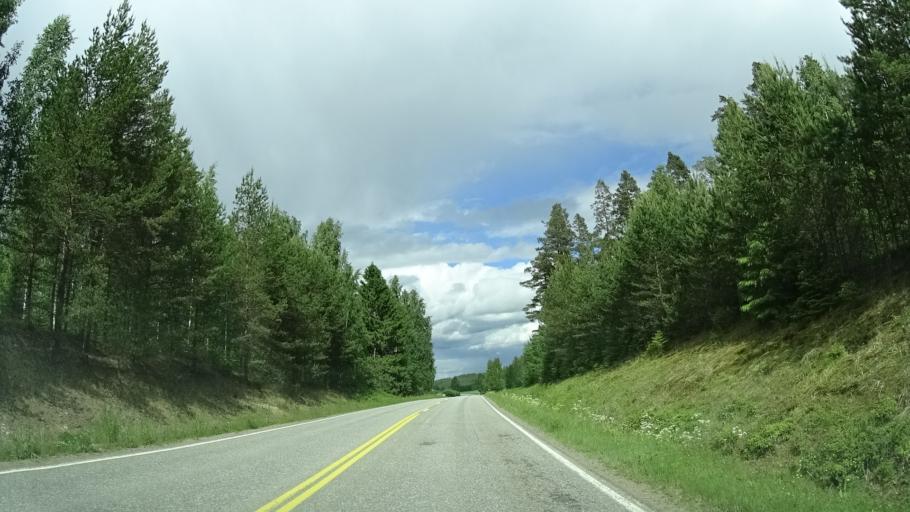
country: FI
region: Paijanne Tavastia
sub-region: Lahti
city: Sysmae
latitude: 61.4073
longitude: 25.6621
